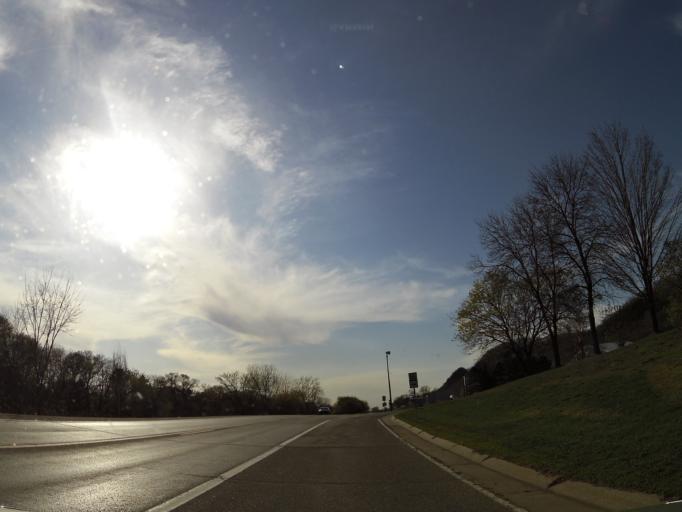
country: US
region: Minnesota
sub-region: Goodhue County
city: Red Wing
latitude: 44.6453
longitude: -92.6135
